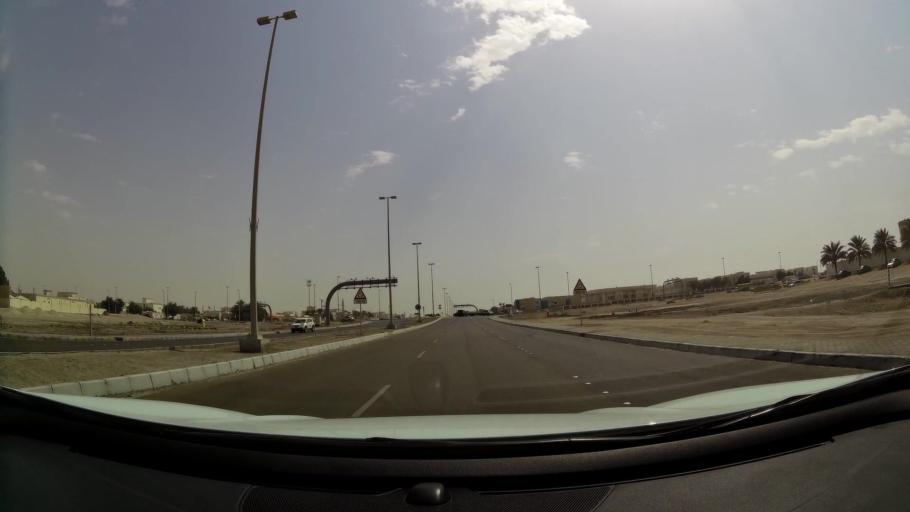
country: AE
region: Abu Dhabi
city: Abu Dhabi
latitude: 24.3020
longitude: 54.6328
